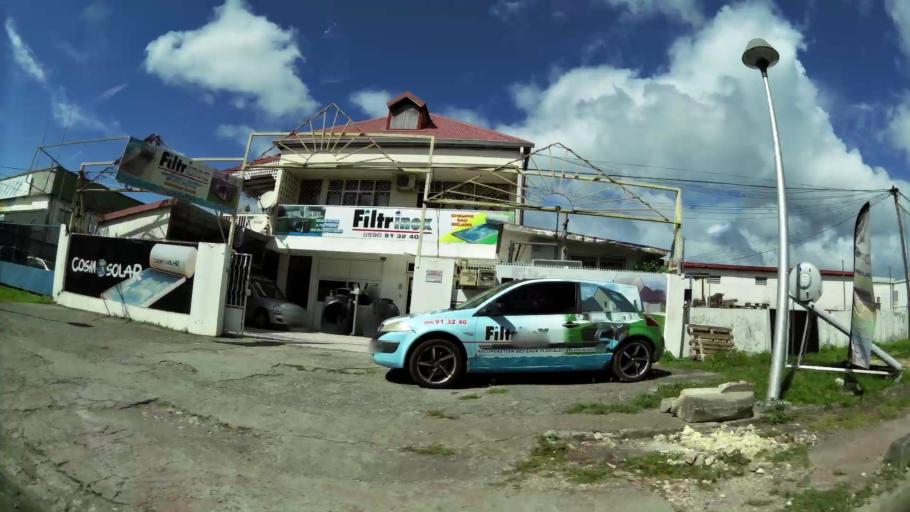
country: GP
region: Guadeloupe
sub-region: Guadeloupe
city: Pointe-a-Pitre
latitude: 16.2466
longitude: -61.5386
